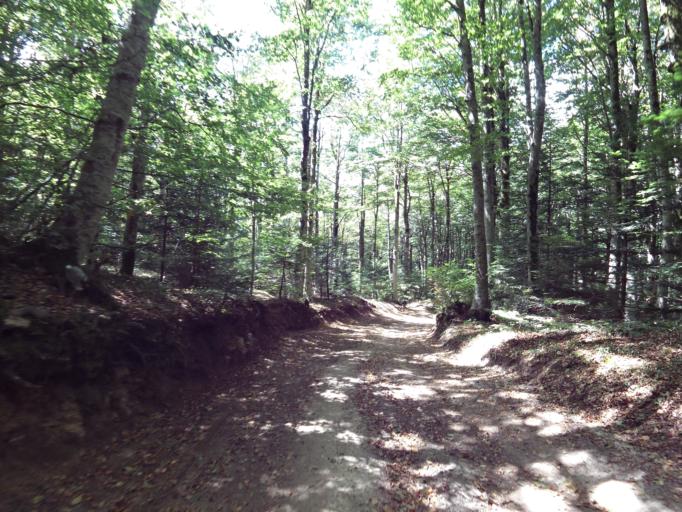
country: IT
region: Calabria
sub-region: Provincia di Vibo-Valentia
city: Mongiana
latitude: 38.5227
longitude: 16.3454
